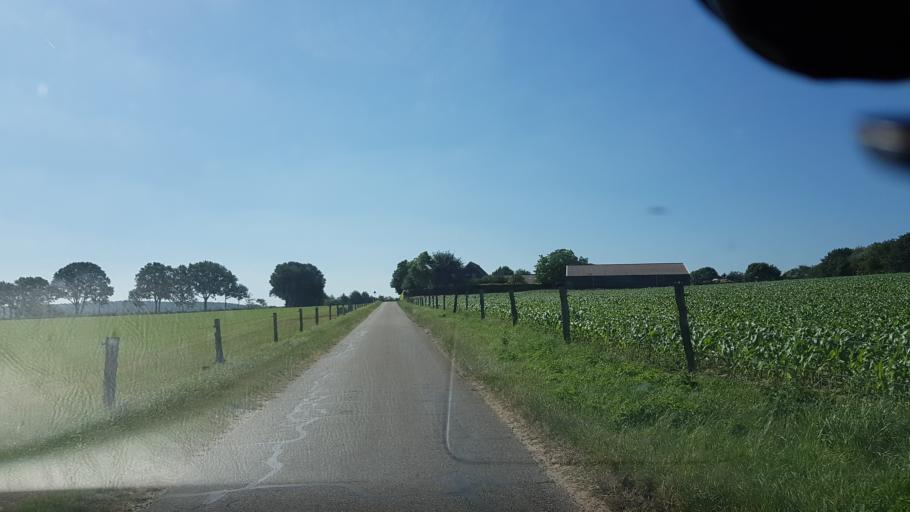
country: NL
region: Gelderland
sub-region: Gemeente Groesbeek
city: Bredeweg
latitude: 51.7531
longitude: 5.9299
